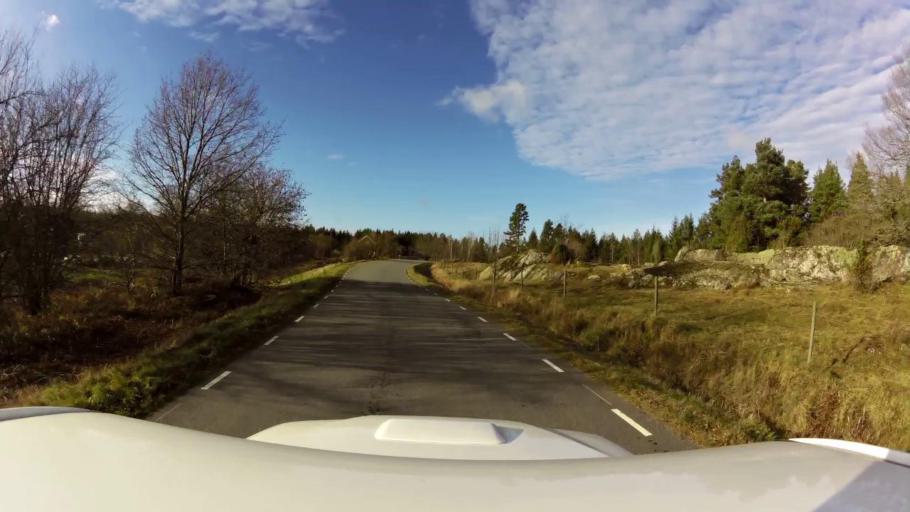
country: SE
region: OEstergoetland
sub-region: Linkopings Kommun
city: Sturefors
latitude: 58.2759
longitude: 15.6589
